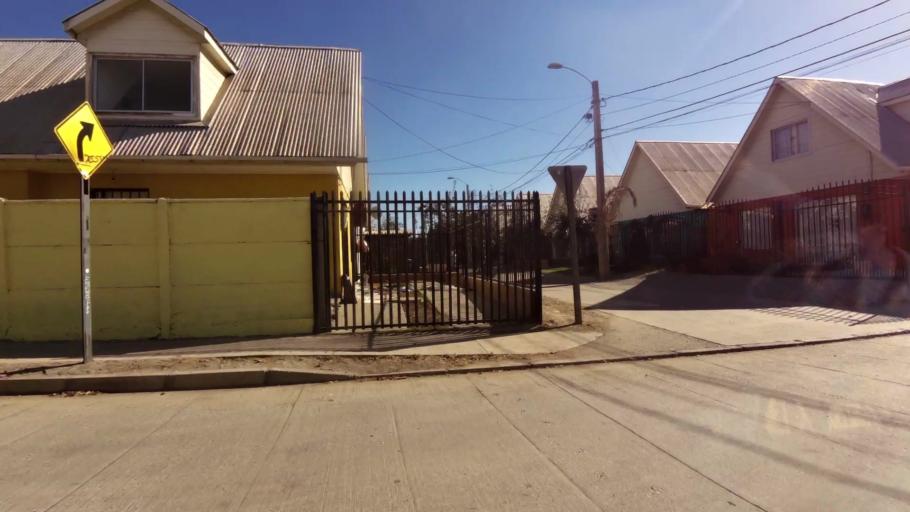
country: CL
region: O'Higgins
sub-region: Provincia de Cachapoal
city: Rancagua
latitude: -34.1798
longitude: -70.7661
